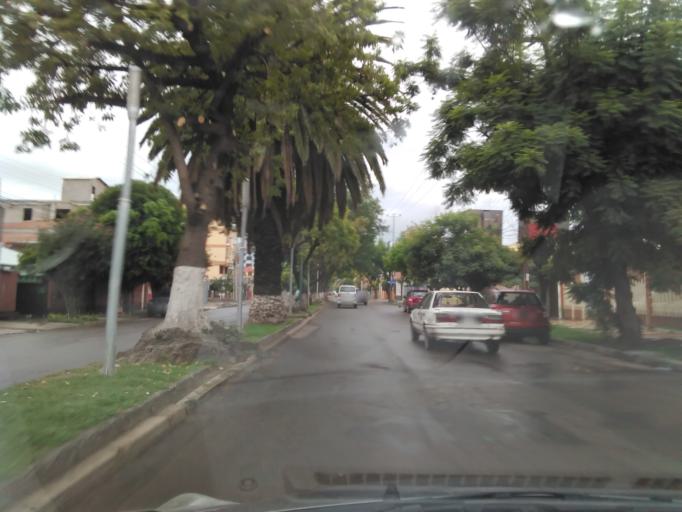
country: BO
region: Cochabamba
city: Cochabamba
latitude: -17.3881
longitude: -66.1663
